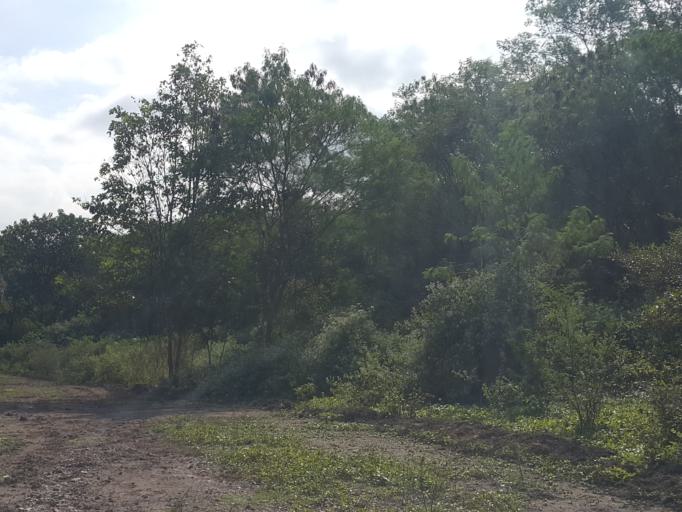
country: TH
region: Lampang
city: Mae Mo
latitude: 18.3430
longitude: 99.7673
